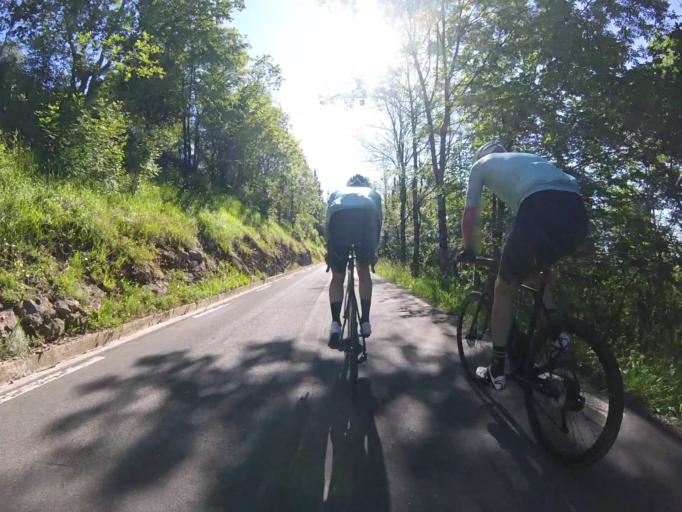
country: ES
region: Basque Country
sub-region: Provincia de Guipuzcoa
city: Beizama
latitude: 43.1245
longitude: -2.1938
